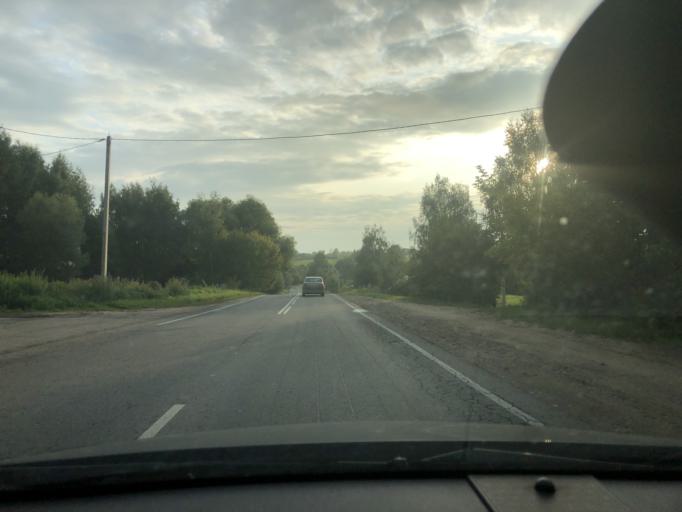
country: RU
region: Tula
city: Leninskiy
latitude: 54.2493
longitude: 37.3453
